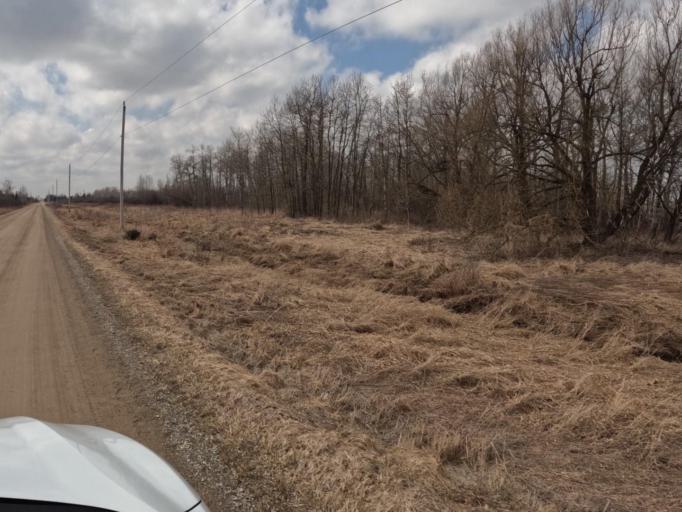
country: CA
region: Ontario
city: Shelburne
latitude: 44.0205
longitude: -80.2975
